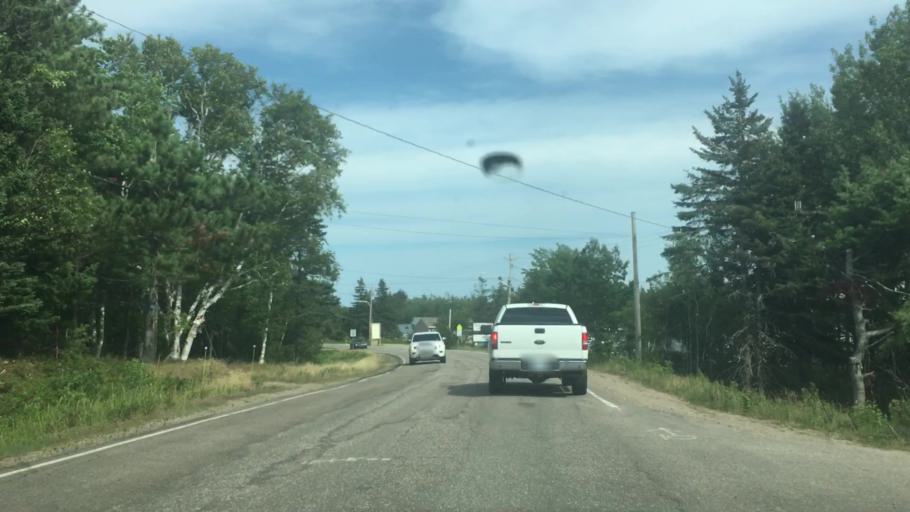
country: CA
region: Nova Scotia
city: Sydney Mines
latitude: 46.6902
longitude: -60.3830
